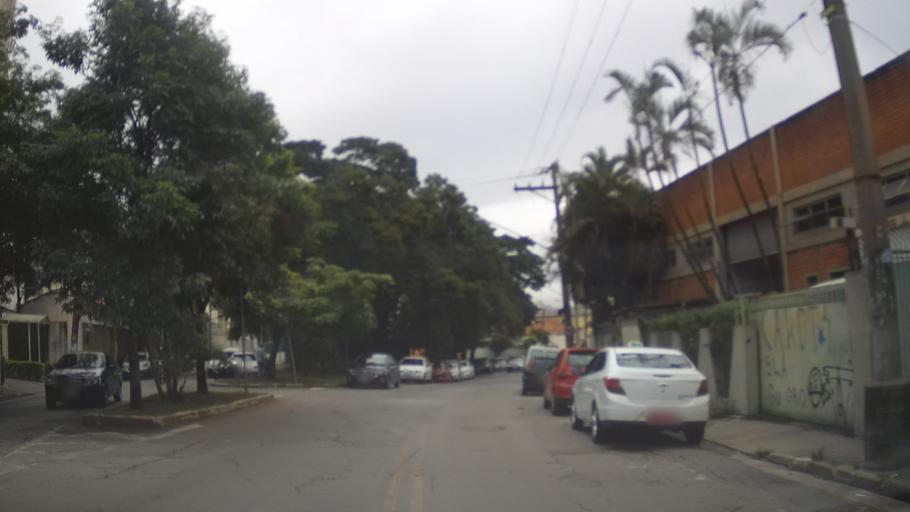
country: BR
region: Sao Paulo
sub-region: Guarulhos
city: Guarulhos
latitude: -23.4847
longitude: -46.5508
